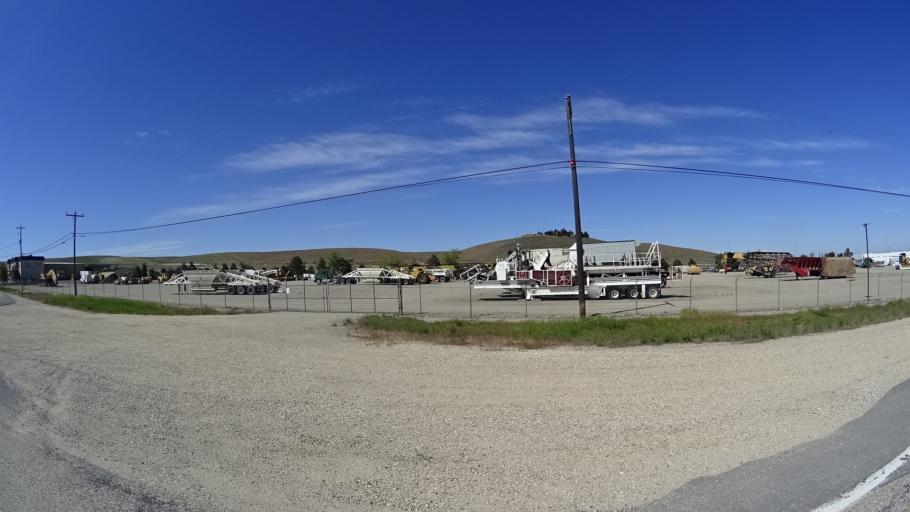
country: US
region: Idaho
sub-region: Ada County
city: Boise
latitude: 43.5121
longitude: -116.1426
